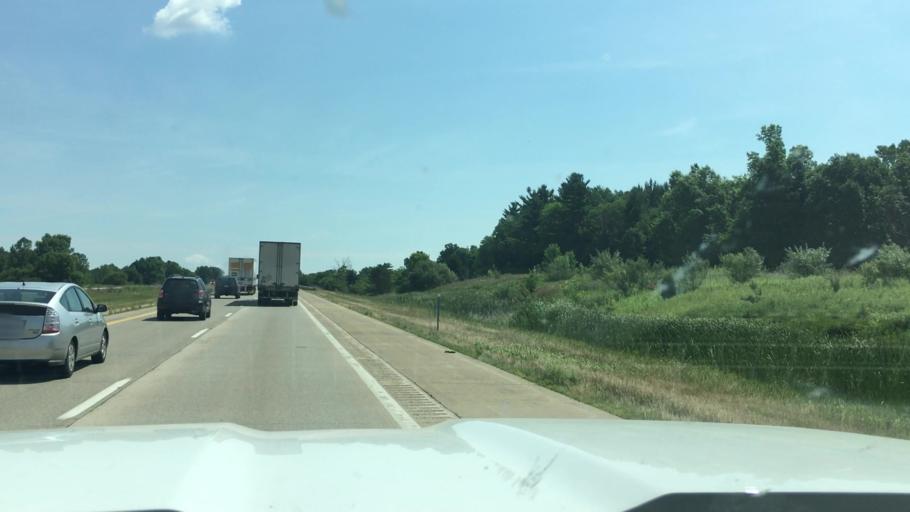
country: US
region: Michigan
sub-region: Shiawassee County
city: Laingsburg
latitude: 42.8042
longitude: -84.3307
